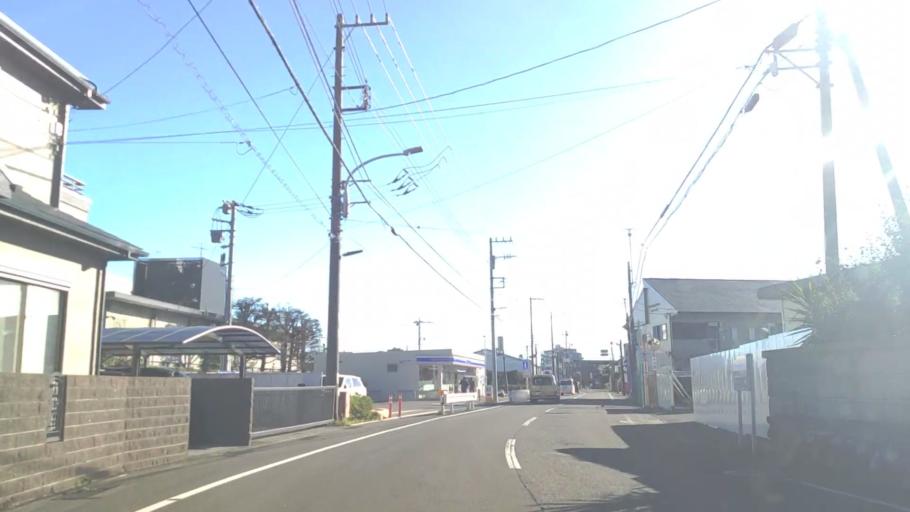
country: JP
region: Kanagawa
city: Atsugi
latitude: 35.3848
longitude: 139.3662
